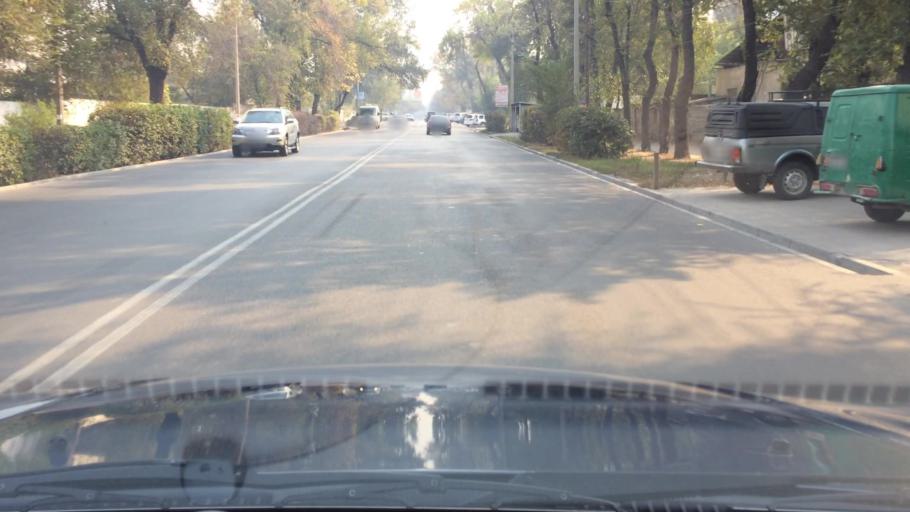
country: KG
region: Chuy
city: Bishkek
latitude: 42.8629
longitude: 74.6023
